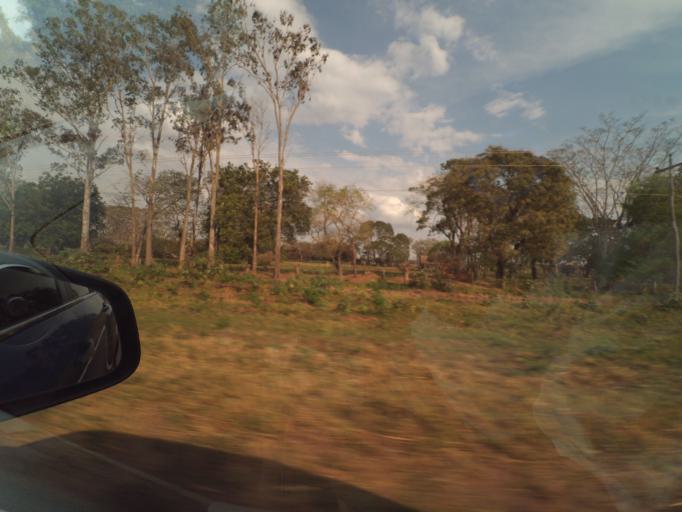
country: BO
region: Santa Cruz
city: Montero
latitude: -17.2698
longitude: -63.0886
